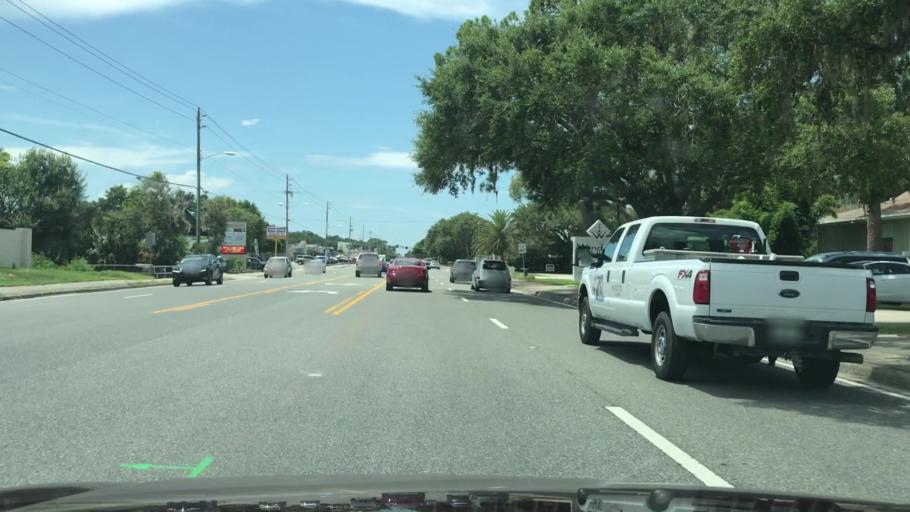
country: US
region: Florida
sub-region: Sarasota County
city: Southgate
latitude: 27.3025
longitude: -82.5142
